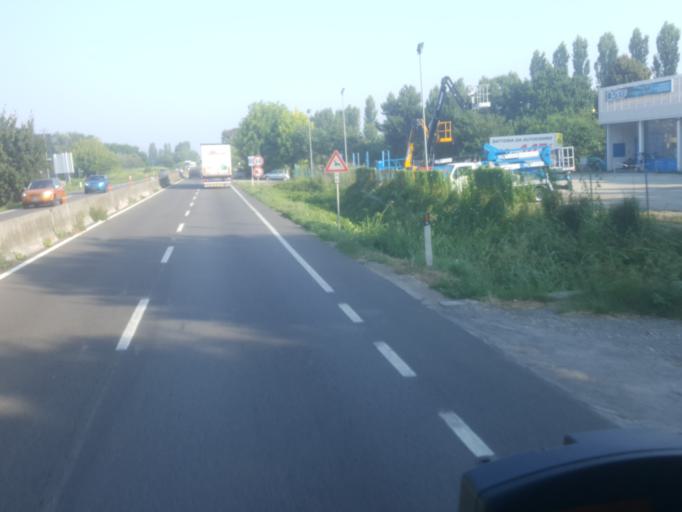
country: IT
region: Emilia-Romagna
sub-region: Provincia di Ravenna
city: Ravenna
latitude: 44.4015
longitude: 12.1793
